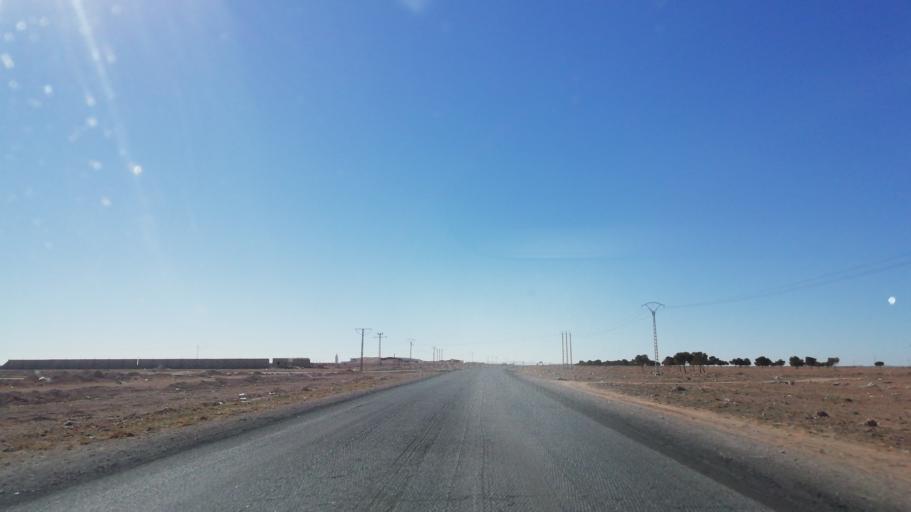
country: DZ
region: Saida
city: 'Ain el Hadjar
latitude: 34.0276
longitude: 0.0710
